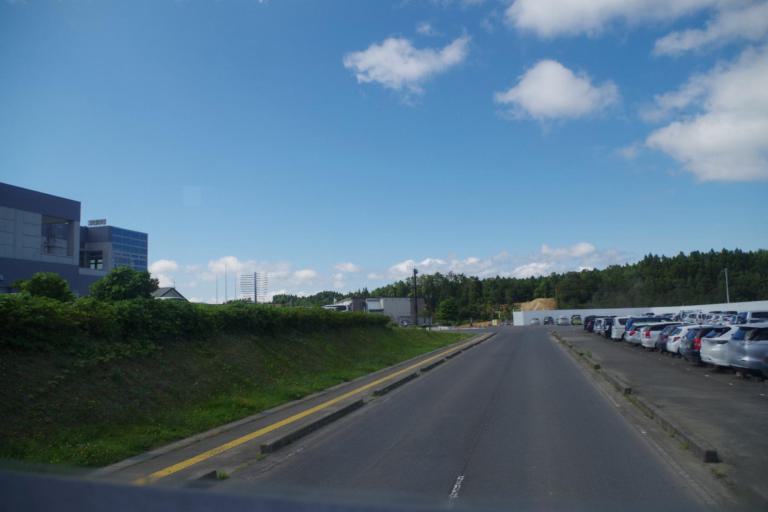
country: JP
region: Miyagi
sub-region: Oshika Gun
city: Onagawa Cho
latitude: 38.6811
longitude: 141.4601
